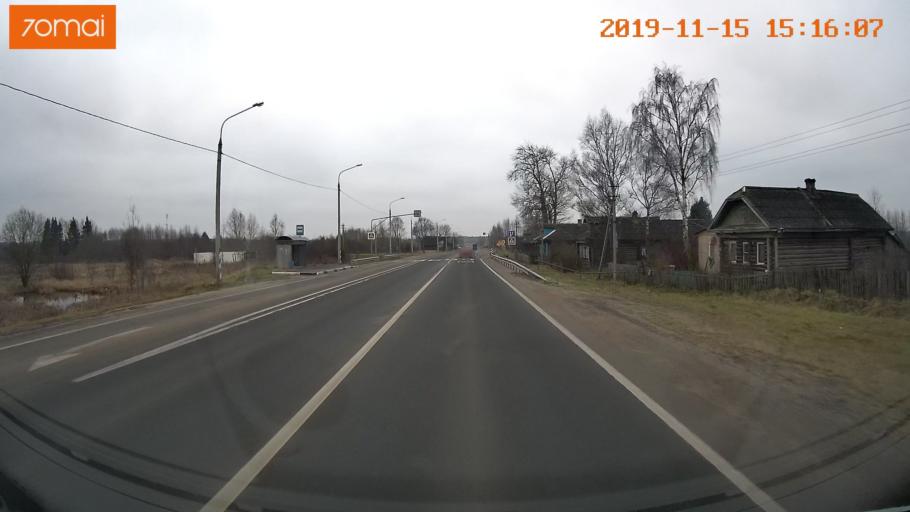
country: RU
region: Jaroslavl
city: Danilov
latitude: 58.2757
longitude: 40.1940
